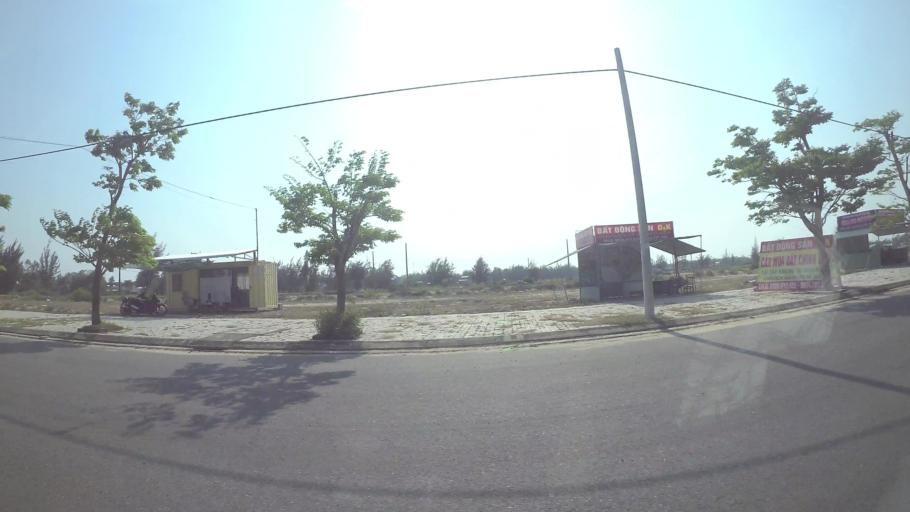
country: VN
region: Da Nang
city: Ngu Hanh Son
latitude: 15.9539
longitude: 108.2743
